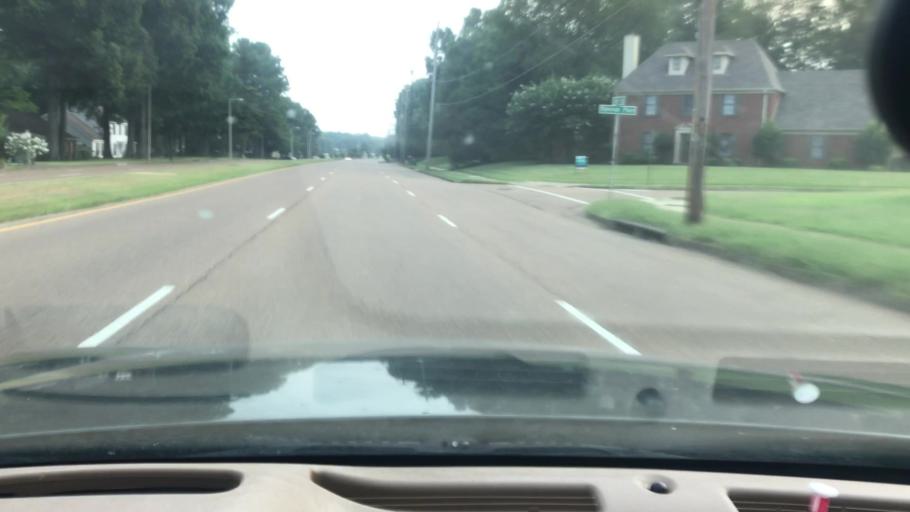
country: US
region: Tennessee
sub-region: Shelby County
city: Bartlett
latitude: 35.1934
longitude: -89.8692
